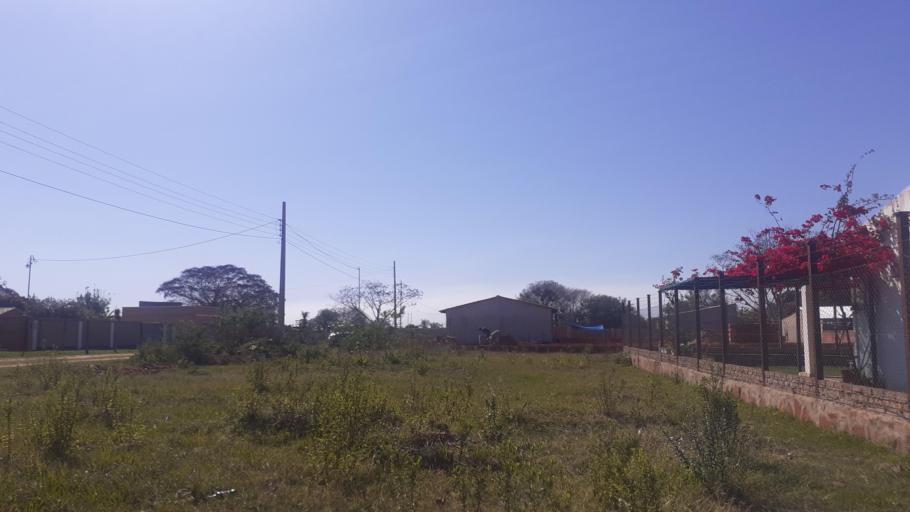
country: PY
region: Misiones
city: San Juan Bautista
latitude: -26.6671
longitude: -57.1281
